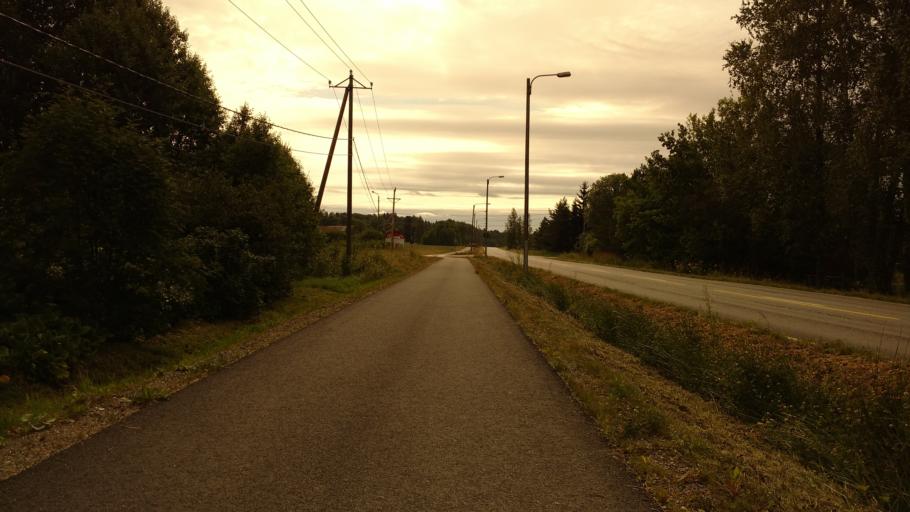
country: FI
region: Varsinais-Suomi
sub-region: Turku
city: Piikkioe
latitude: 60.4299
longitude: 22.4768
